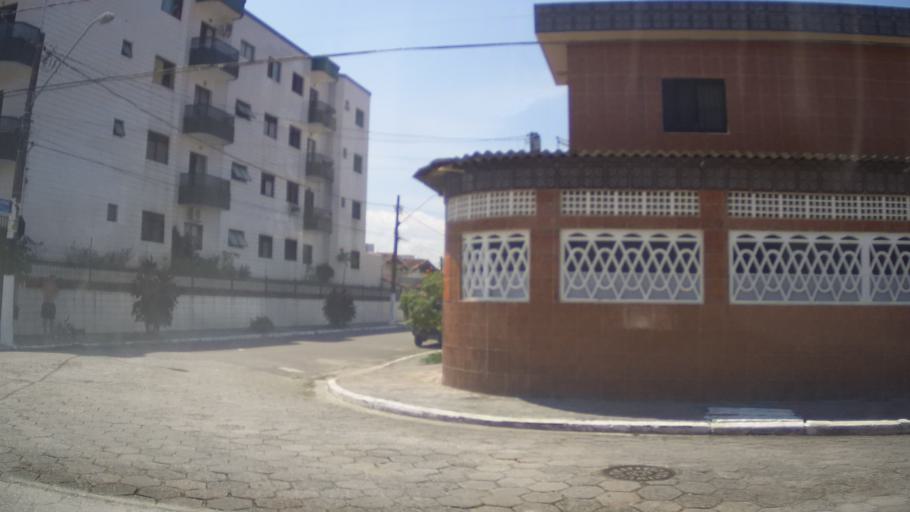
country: BR
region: Sao Paulo
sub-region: Praia Grande
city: Praia Grande
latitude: -24.0106
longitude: -46.4342
